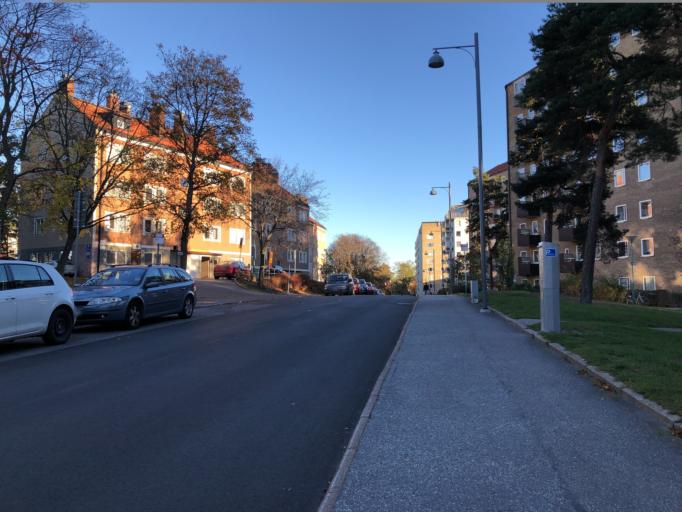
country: SE
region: Stockholm
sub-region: Solna Kommun
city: Rasunda
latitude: 59.3663
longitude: 17.9784
